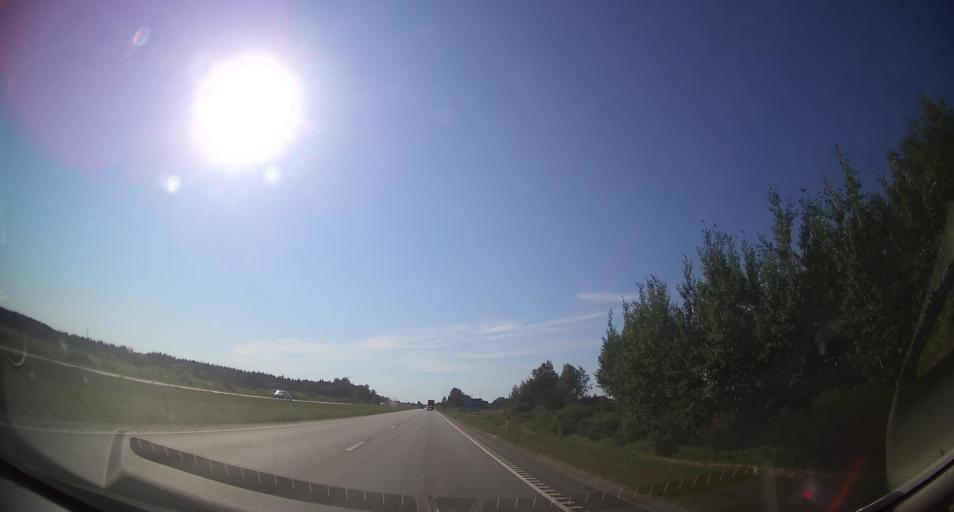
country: EE
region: Harju
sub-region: Raasiku vald
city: Raasiku
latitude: 59.4349
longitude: 25.1592
